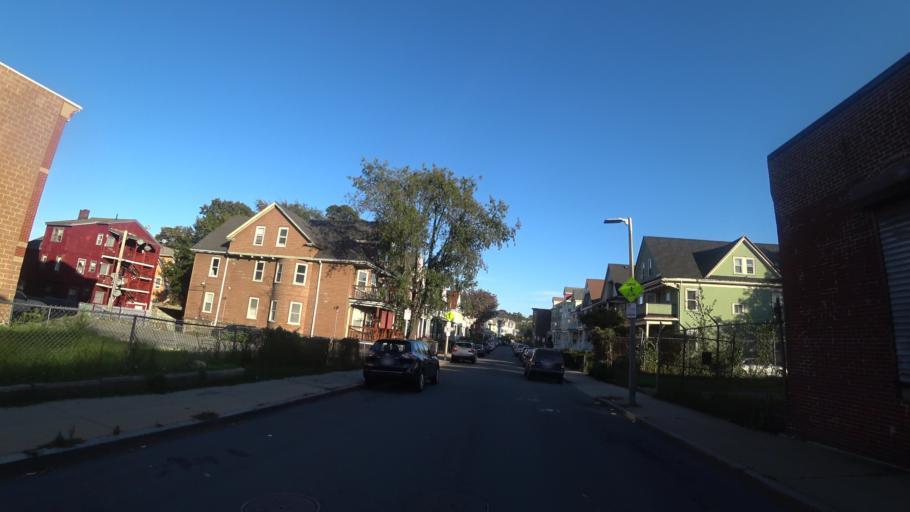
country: US
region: Massachusetts
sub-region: Suffolk County
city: Jamaica Plain
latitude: 42.3108
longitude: -71.0815
